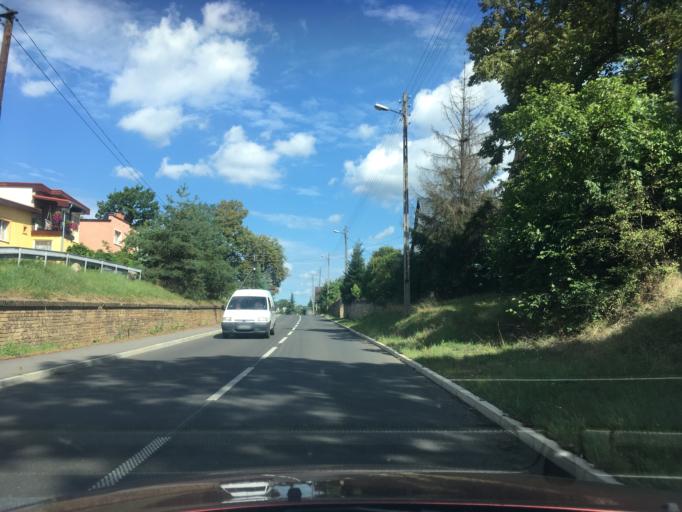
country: PL
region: Lower Silesian Voivodeship
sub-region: Powiat zgorzelecki
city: Piensk
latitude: 51.2558
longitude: 15.0441
